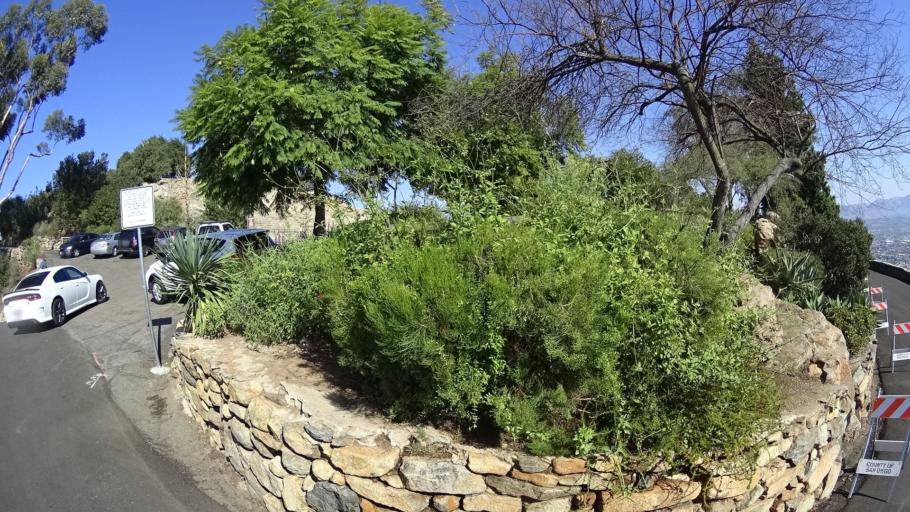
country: US
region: California
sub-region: San Diego County
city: Casa de Oro-Mount Helix
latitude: 32.7667
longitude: -116.9826
